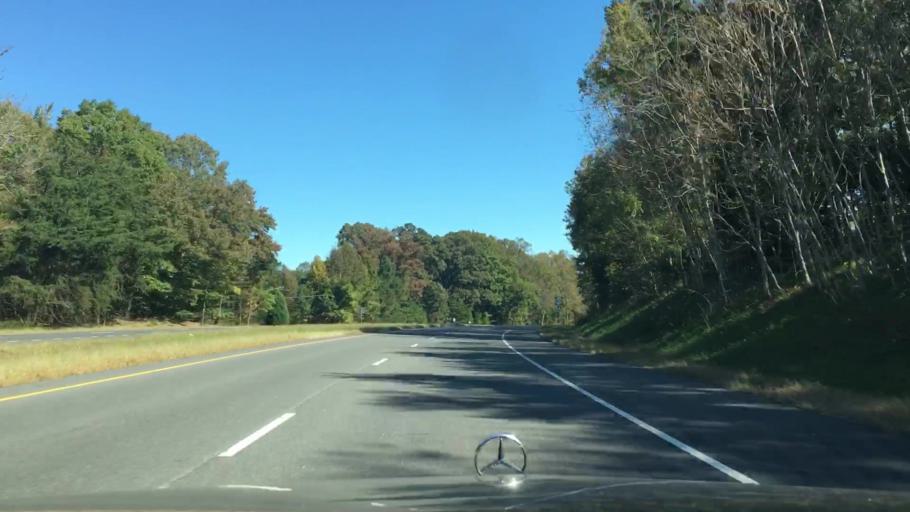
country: US
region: Virginia
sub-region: King George County
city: King George
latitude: 38.2772
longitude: -77.2310
